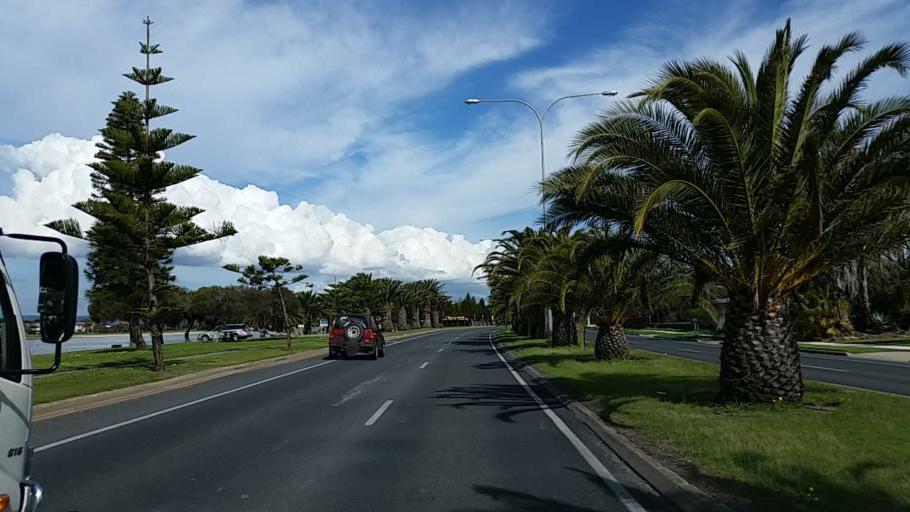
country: AU
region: South Australia
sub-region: Charles Sturt
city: Grange
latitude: -34.8853
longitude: 138.4864
